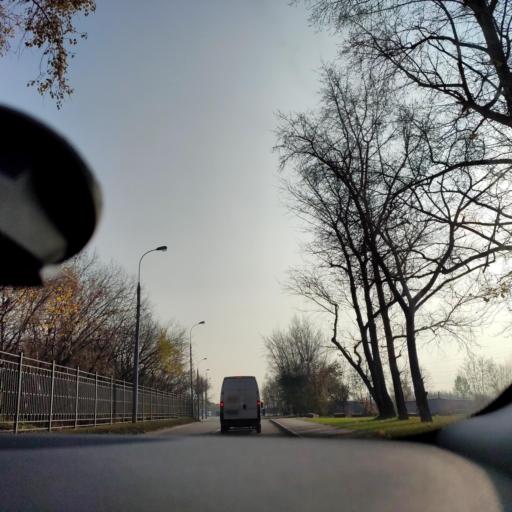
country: RU
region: Moscow
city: Kuz'minki
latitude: 55.6770
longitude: 37.7940
